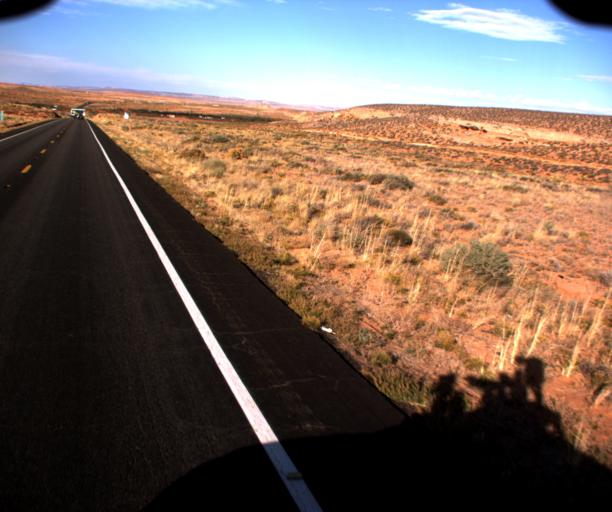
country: US
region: Arizona
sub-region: Apache County
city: Many Farms
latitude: 36.9252
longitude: -109.5929
